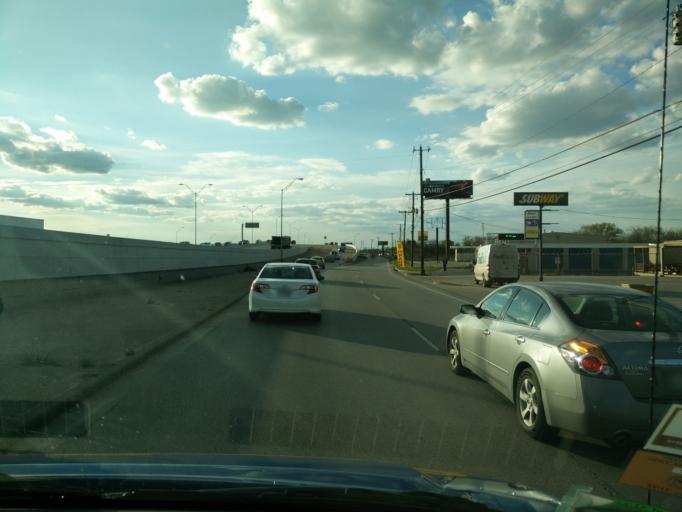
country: US
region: Texas
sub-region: Travis County
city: Hornsby Bend
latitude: 30.2142
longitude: -97.6607
